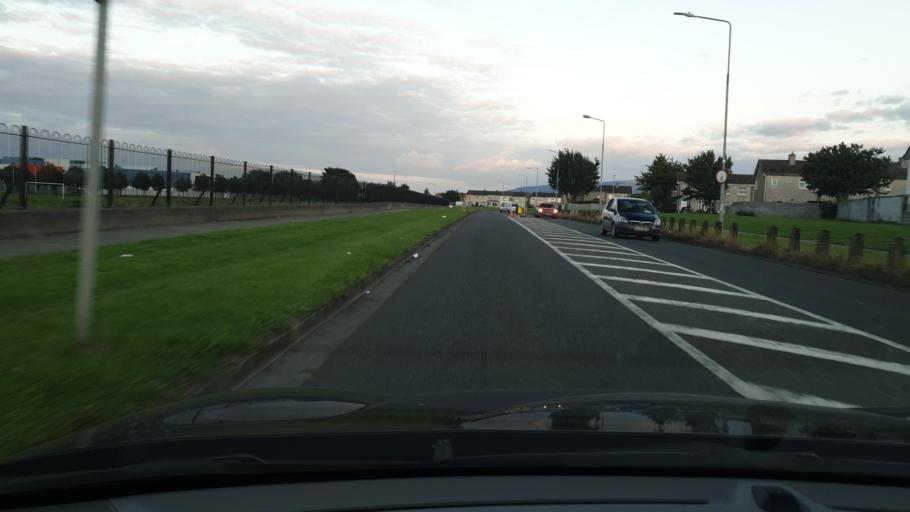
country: IE
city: Jobstown
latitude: 53.2828
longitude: -6.3973
